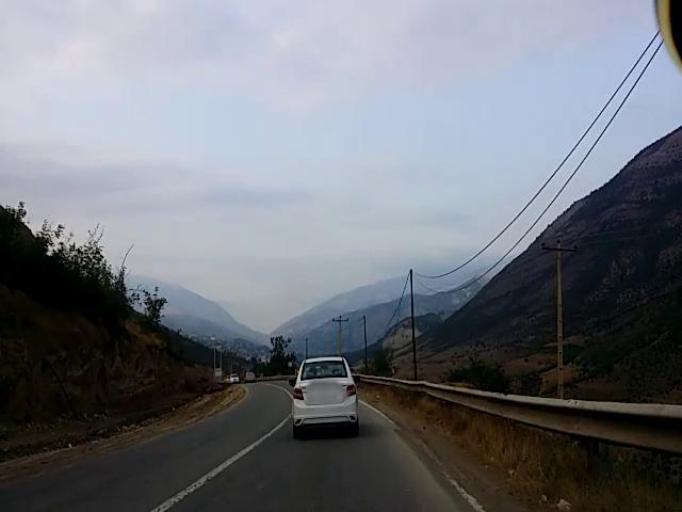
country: IR
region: Mazandaran
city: Chalus
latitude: 36.4230
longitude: 51.2825
